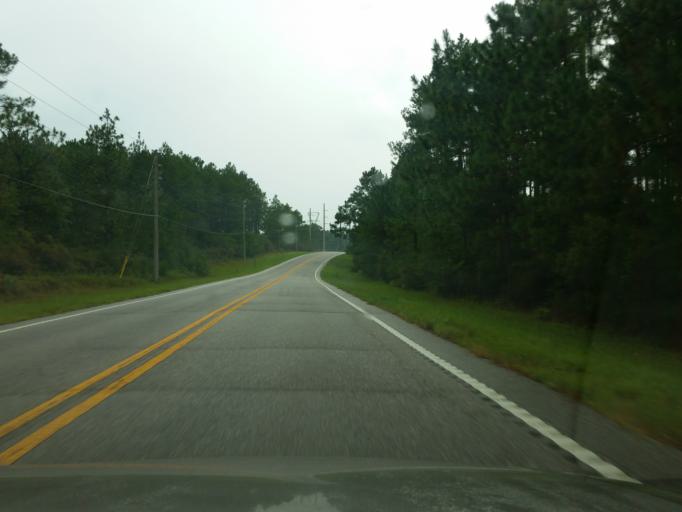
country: US
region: Alabama
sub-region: Baldwin County
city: Elberta
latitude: 30.5267
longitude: -87.5102
